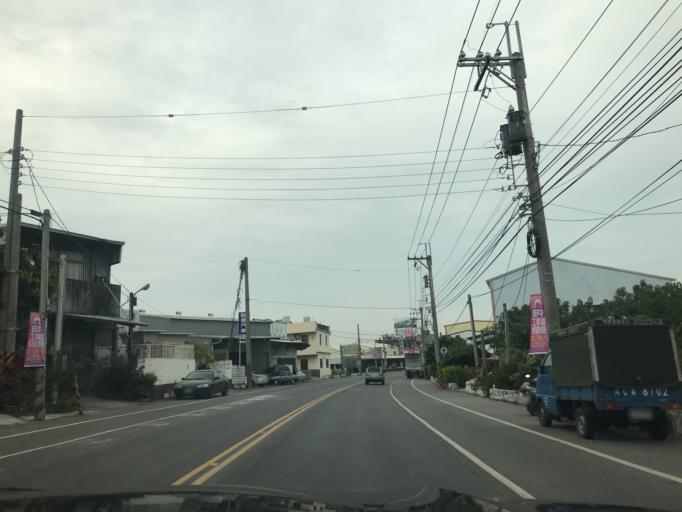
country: TW
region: Taiwan
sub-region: Nantou
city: Nantou
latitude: 23.9207
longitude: 120.5827
